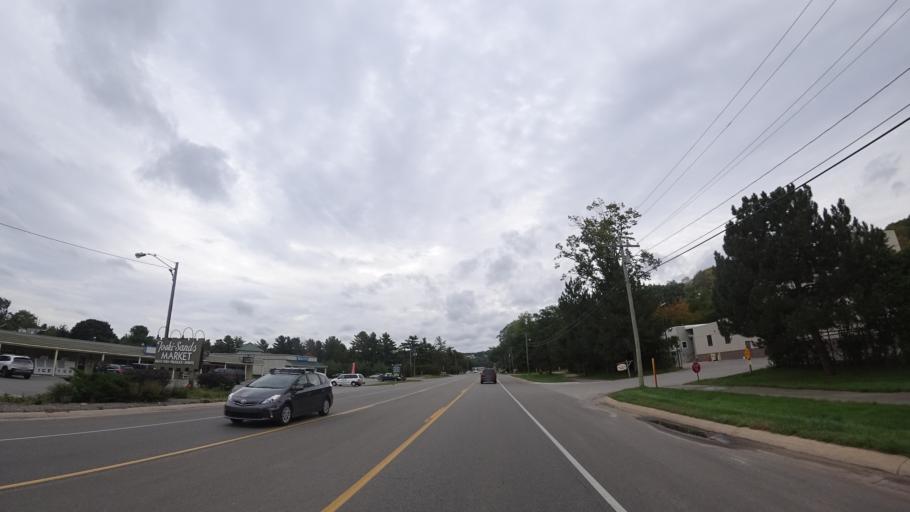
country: US
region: Michigan
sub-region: Emmet County
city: Petoskey
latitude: 45.4038
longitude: -84.9021
